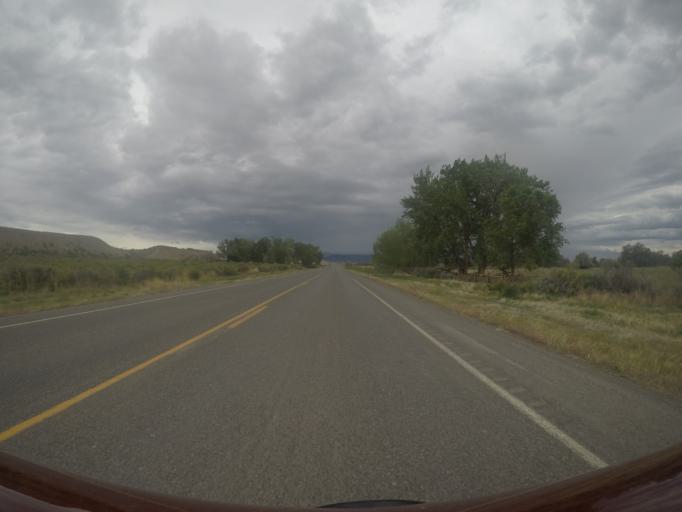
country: US
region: Wyoming
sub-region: Big Horn County
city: Lovell
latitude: 44.8666
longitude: -108.3277
